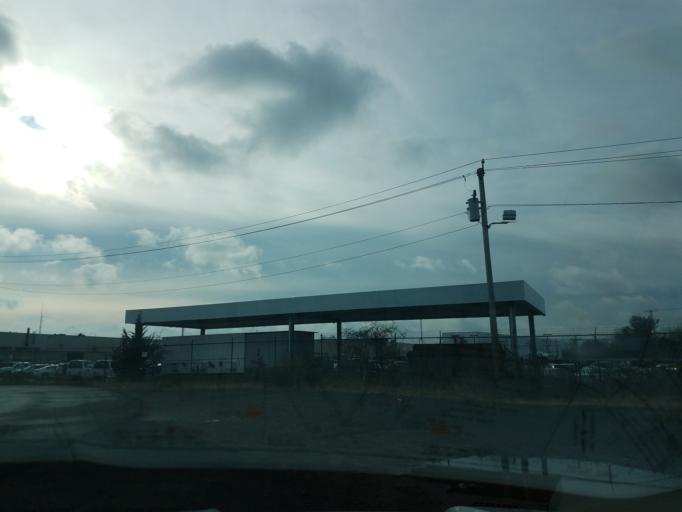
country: US
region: Connecticut
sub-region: New Haven County
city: New Haven
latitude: 41.2905
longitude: -72.9263
